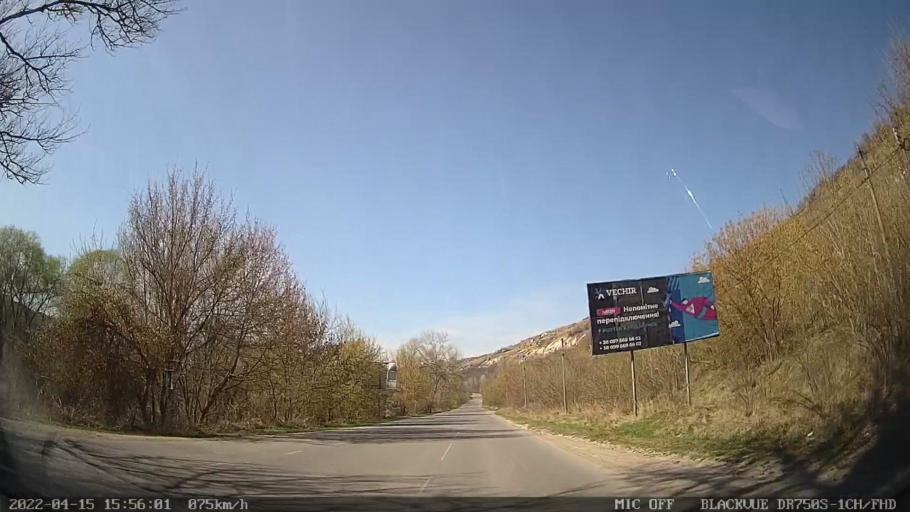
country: MD
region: Raionul Ocnita
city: Otaci
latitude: 48.4020
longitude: 27.8770
